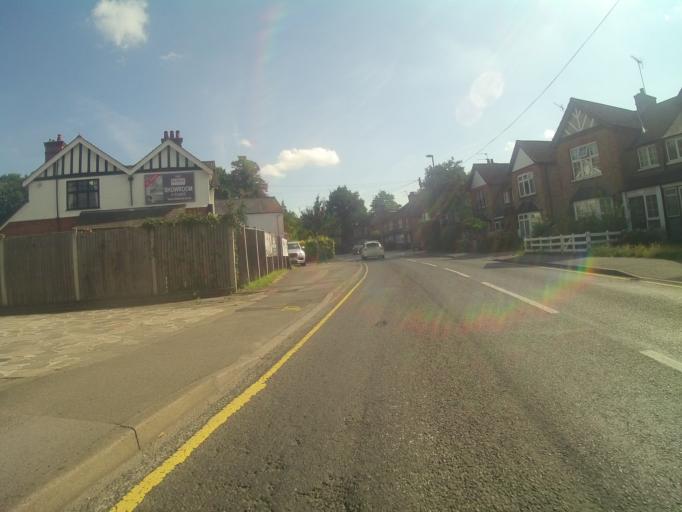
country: GB
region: England
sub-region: Surrey
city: Woking
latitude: 51.3131
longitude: -0.5748
